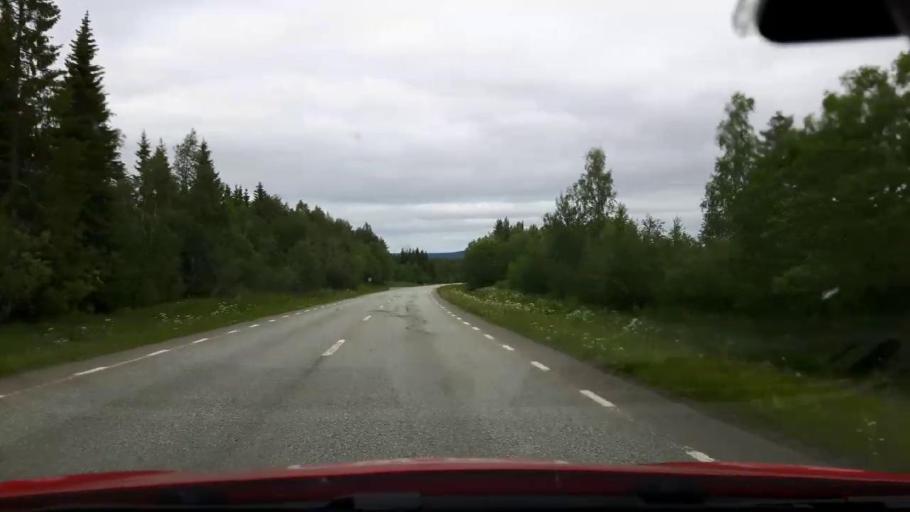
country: SE
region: Jaemtland
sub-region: Krokoms Kommun
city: Krokom
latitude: 63.5864
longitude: 14.6366
